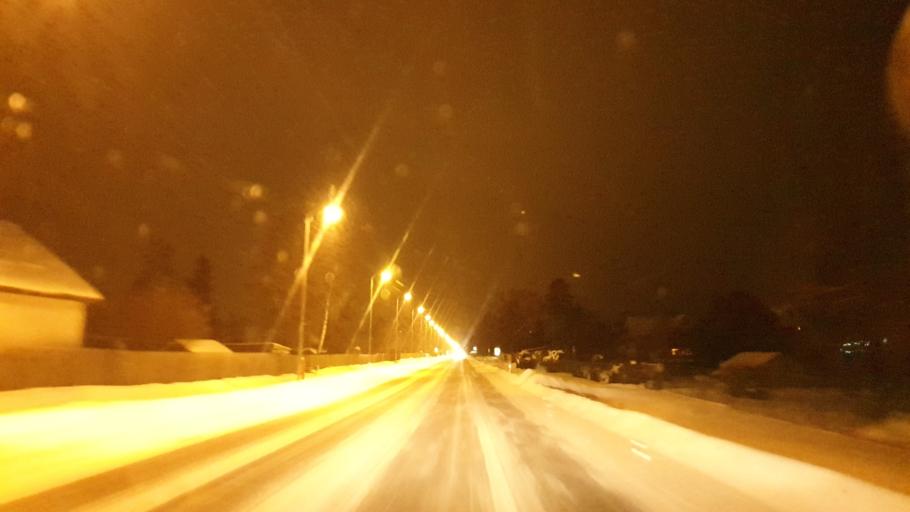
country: EE
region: Harju
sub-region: Viimsi vald
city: Viimsi
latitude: 59.5008
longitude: 24.9040
